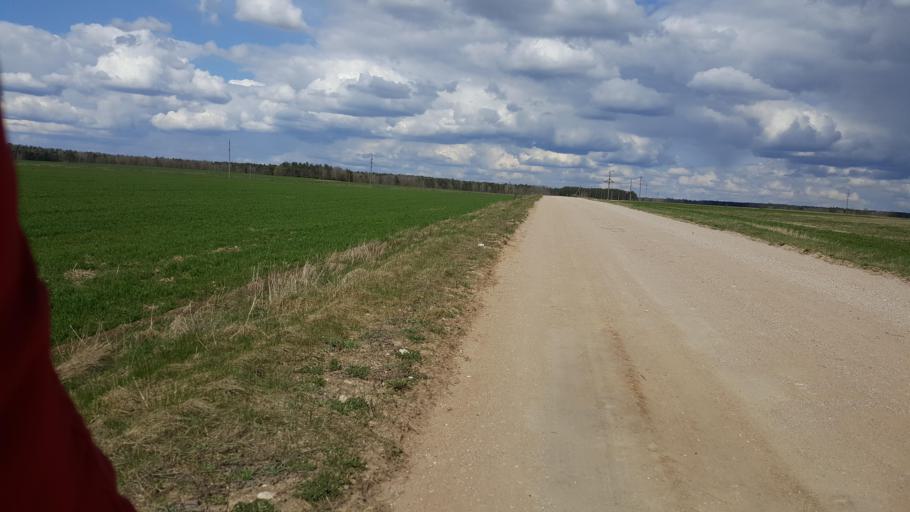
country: BY
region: Brest
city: Kamyanyets
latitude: 52.3762
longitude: 23.6610
